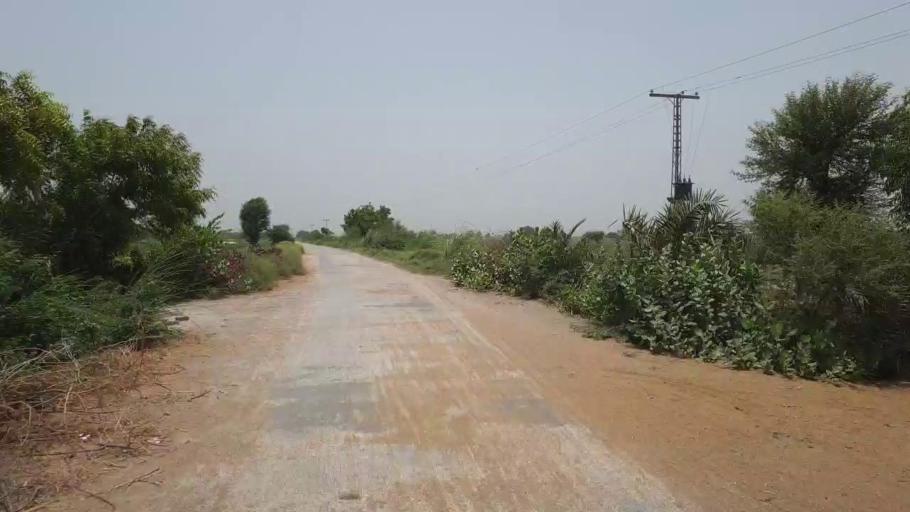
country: PK
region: Sindh
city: Tando Mittha Khan
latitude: 26.0655
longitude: 69.2061
